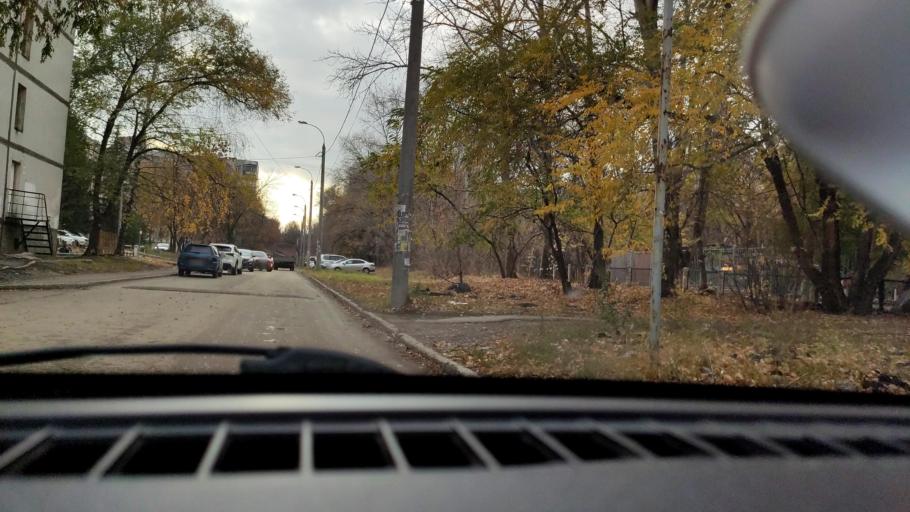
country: RU
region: Samara
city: Samara
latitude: 53.2384
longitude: 50.2116
